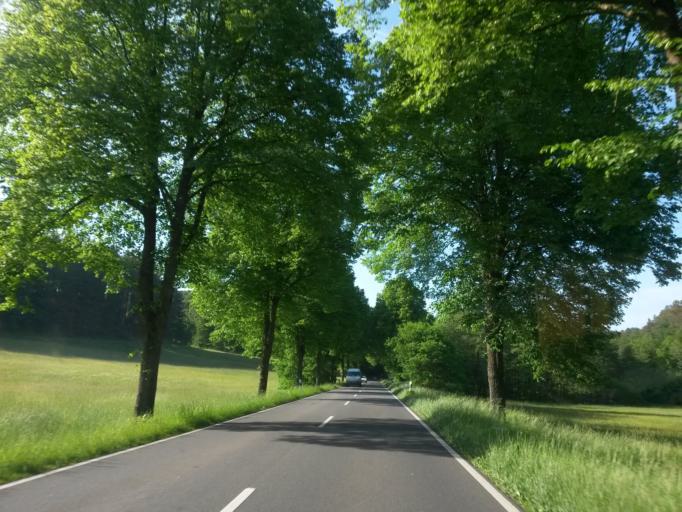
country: DE
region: North Rhine-Westphalia
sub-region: Regierungsbezirk Koln
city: Hennef
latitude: 50.8502
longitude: 7.3195
